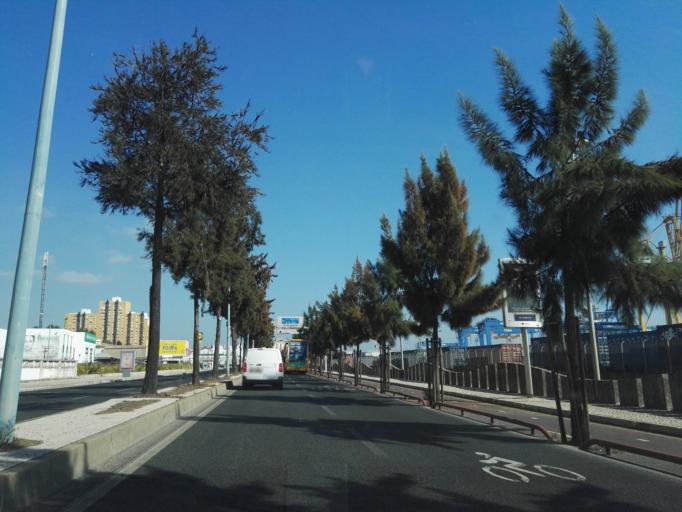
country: PT
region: Lisbon
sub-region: Lisbon
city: Lisbon
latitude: 38.7233
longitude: -9.1129
